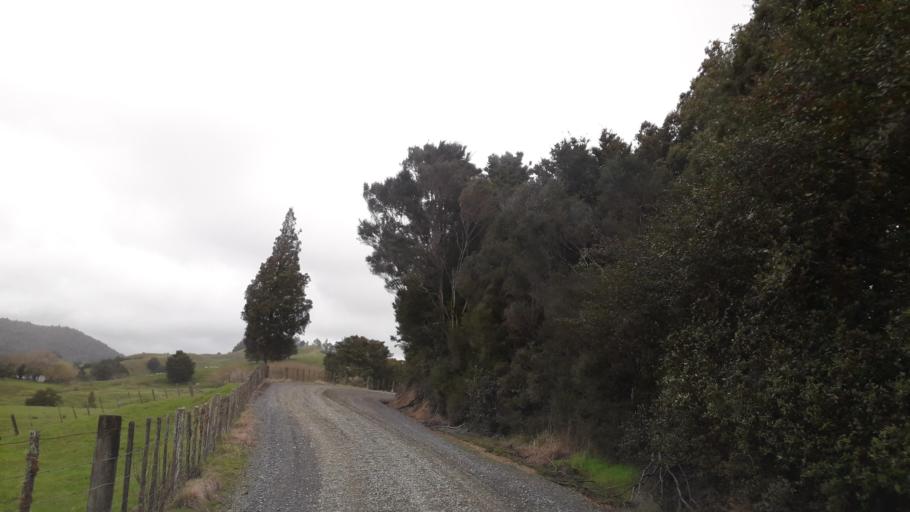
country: NZ
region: Northland
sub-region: Far North District
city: Waimate North
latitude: -35.1375
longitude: 173.7129
